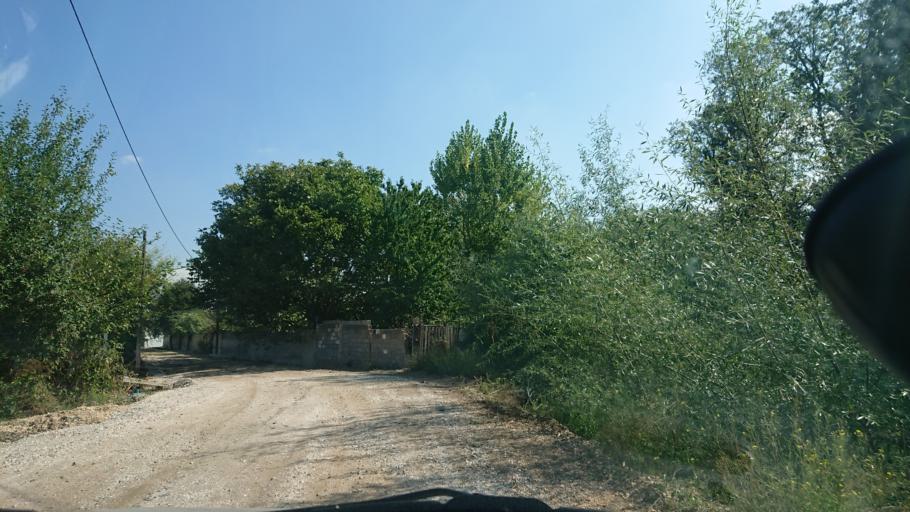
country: TR
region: Eskisehir
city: Eskisehir
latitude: 39.7539
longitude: 30.4746
